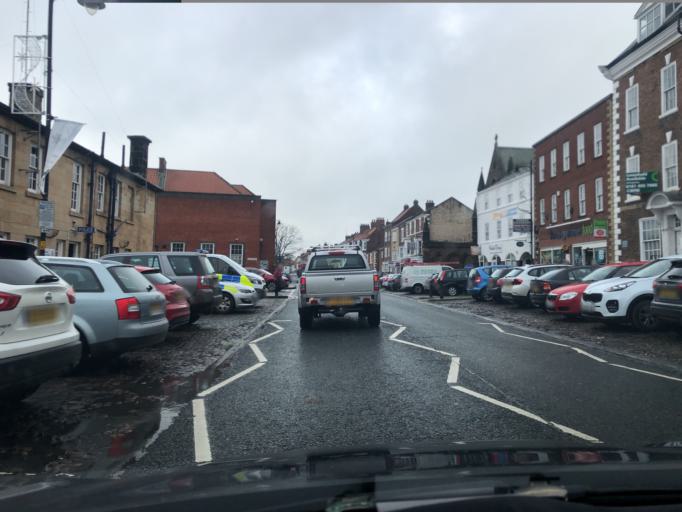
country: GB
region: England
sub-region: North Yorkshire
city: Stokesley
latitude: 54.4699
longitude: -1.1930
